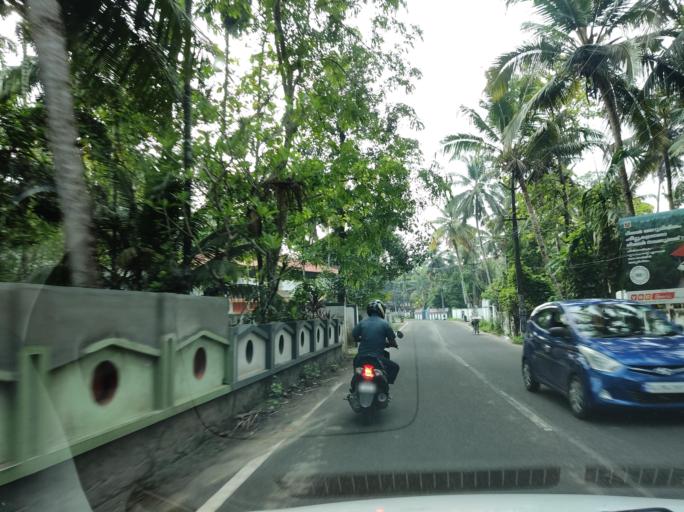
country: IN
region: Kerala
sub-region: Alappuzha
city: Kayankulam
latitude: 9.1772
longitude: 76.4906
